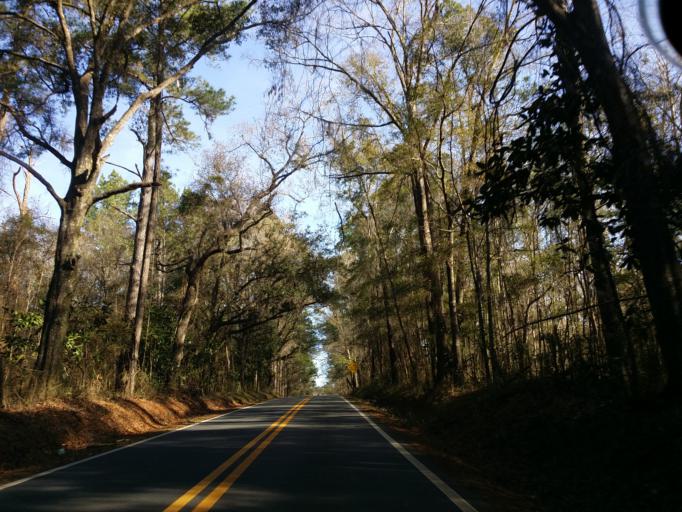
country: US
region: Florida
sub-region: Leon County
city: Woodville
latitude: 30.3897
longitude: -84.1553
